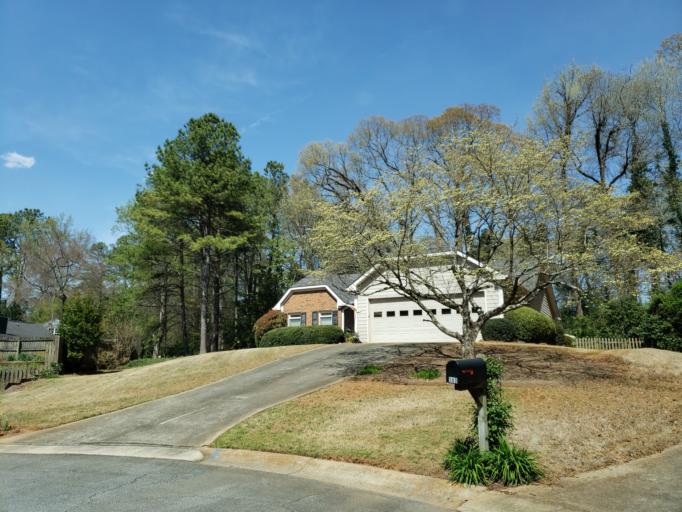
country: US
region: Georgia
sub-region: Cobb County
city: Marietta
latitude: 33.9661
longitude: -84.5597
